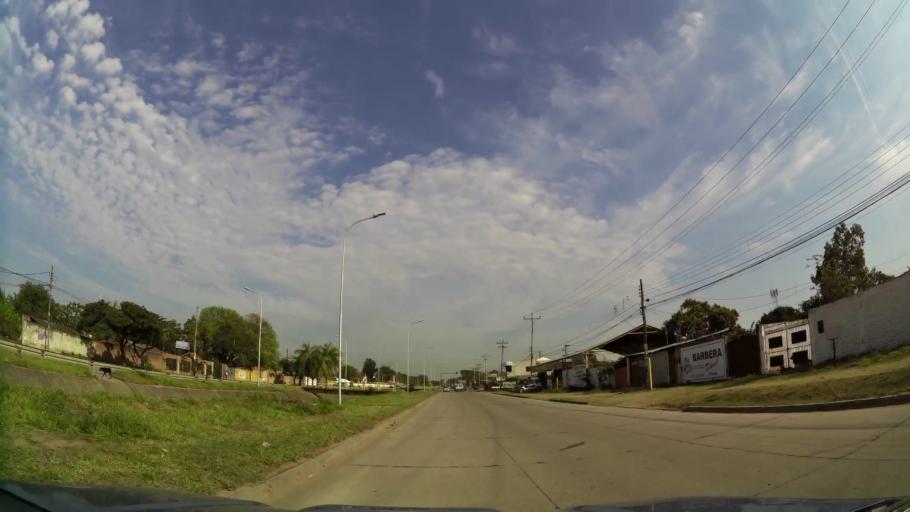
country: BO
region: Santa Cruz
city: Santa Cruz de la Sierra
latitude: -17.7354
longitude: -63.1588
